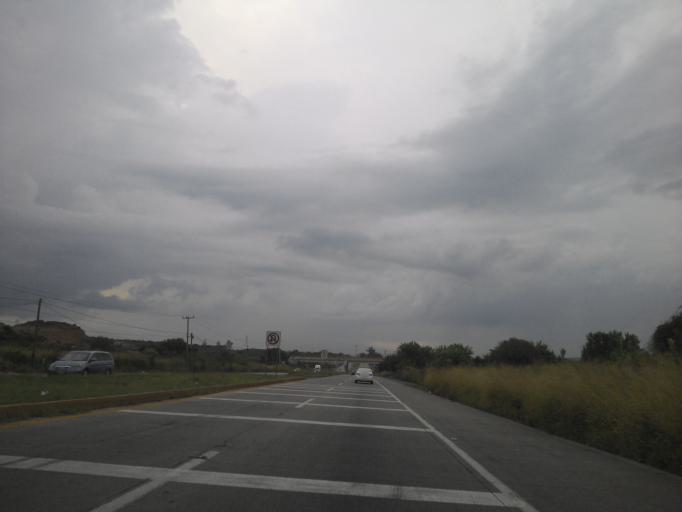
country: MX
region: Jalisco
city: Zapotlanejo
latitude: 20.6011
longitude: -103.0987
